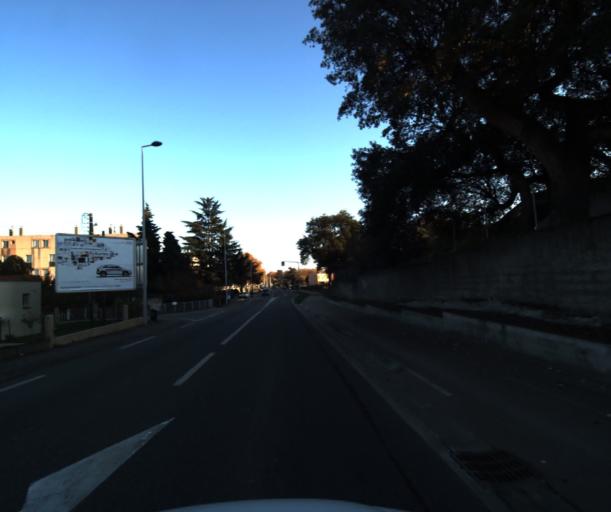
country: FR
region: Midi-Pyrenees
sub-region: Departement de la Haute-Garonne
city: Colomiers
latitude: 43.6119
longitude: 1.3445
